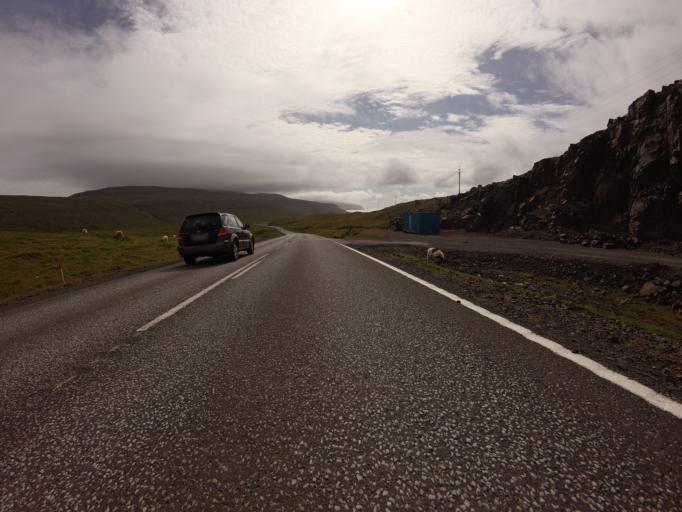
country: FO
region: Sandoy
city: Sandur
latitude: 61.8730
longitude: -6.8548
